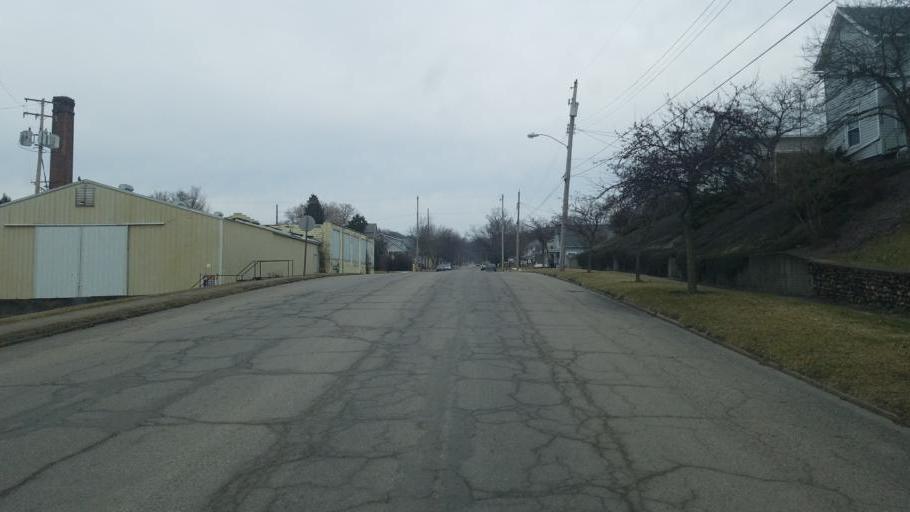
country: US
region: Ohio
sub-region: Ashland County
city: Loudonville
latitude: 40.6383
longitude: -82.2333
